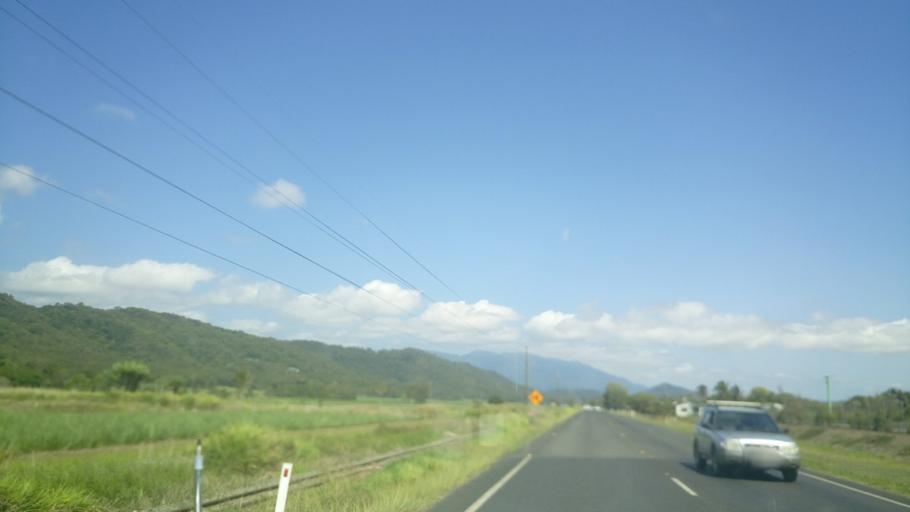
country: AU
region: Queensland
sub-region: Cairns
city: Port Douglas
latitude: -16.5055
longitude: 145.4377
